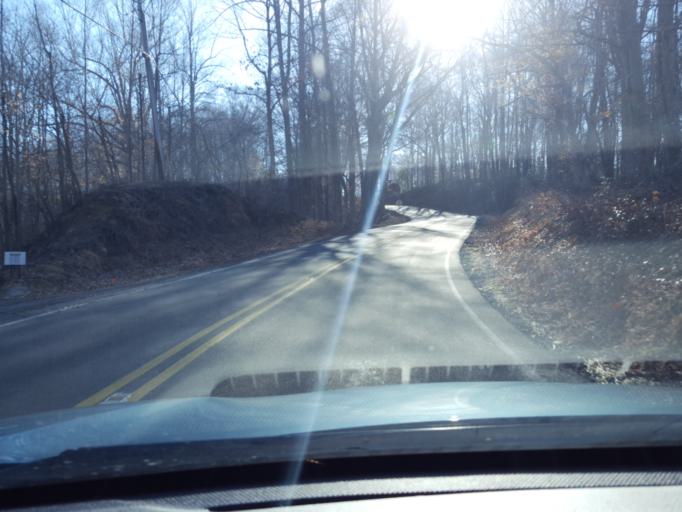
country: US
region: Maryland
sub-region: Calvert County
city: Chesapeake Beach
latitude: 38.6514
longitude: -76.5695
